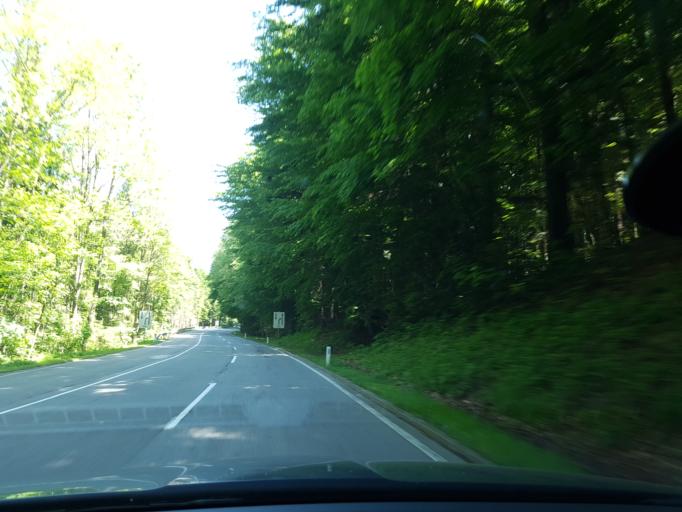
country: AT
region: Salzburg
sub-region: Politischer Bezirk Salzburg-Umgebung
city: Mattsee
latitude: 47.9670
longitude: 13.1154
